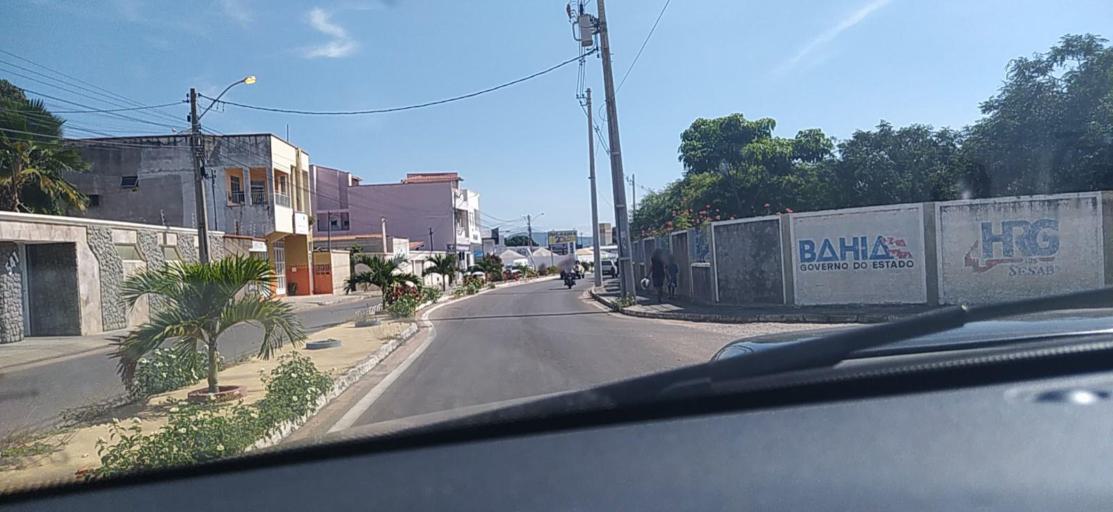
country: BR
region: Bahia
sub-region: Guanambi
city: Guanambi
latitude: -14.2140
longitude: -42.7663
